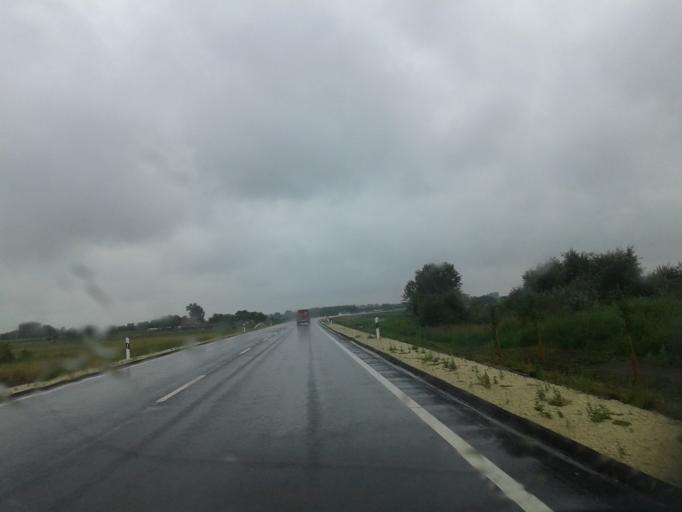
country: HU
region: Csongrad
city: Morahalom
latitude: 46.2325
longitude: 19.8490
